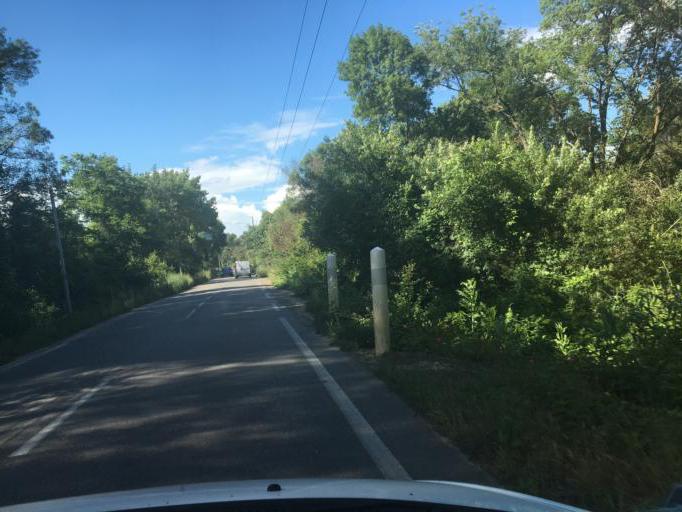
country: FR
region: Provence-Alpes-Cote d'Azur
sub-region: Departement des Bouches-du-Rhone
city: Eguilles
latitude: 43.5262
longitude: 5.3517
